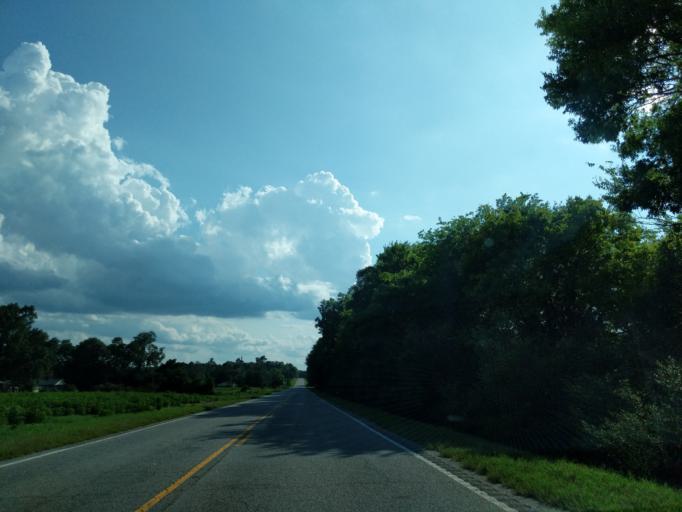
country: US
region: South Carolina
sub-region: Barnwell County
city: Williston
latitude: 33.4485
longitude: -81.3668
